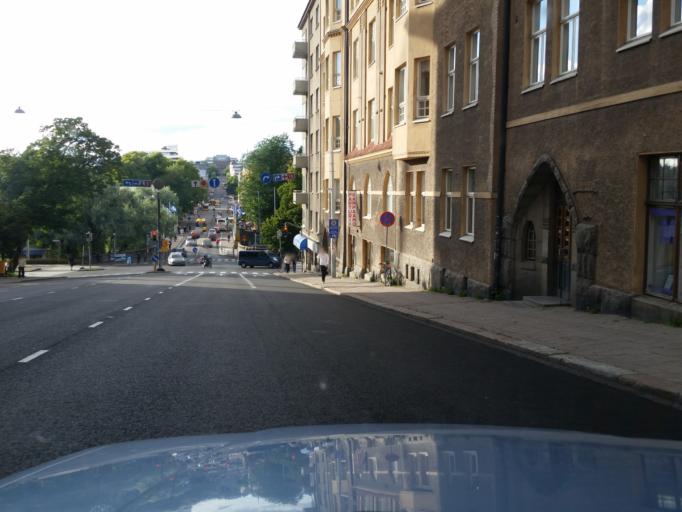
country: FI
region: Varsinais-Suomi
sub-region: Turku
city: Turku
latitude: 60.4476
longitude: 22.2714
